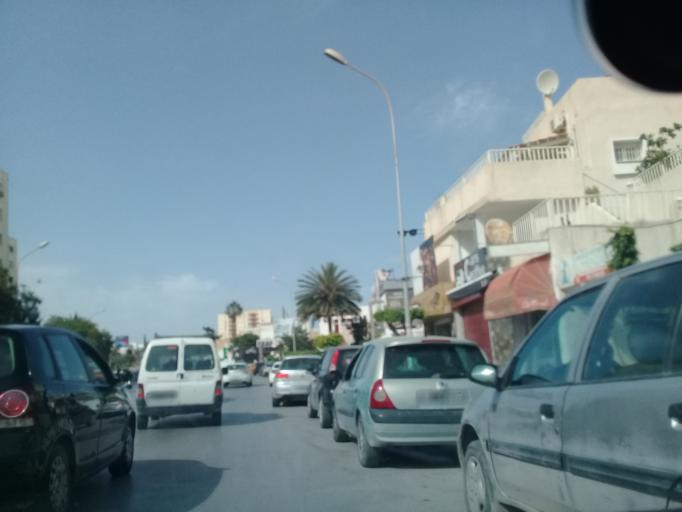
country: TN
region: Tunis
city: Tunis
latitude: 36.8443
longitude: 10.1662
